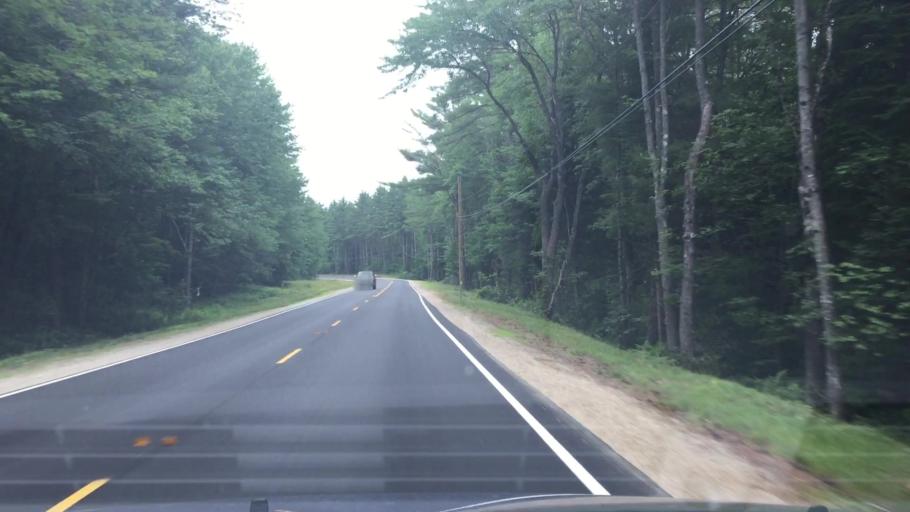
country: US
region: New Hampshire
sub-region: Carroll County
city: Freedom
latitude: 43.8306
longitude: -71.0767
